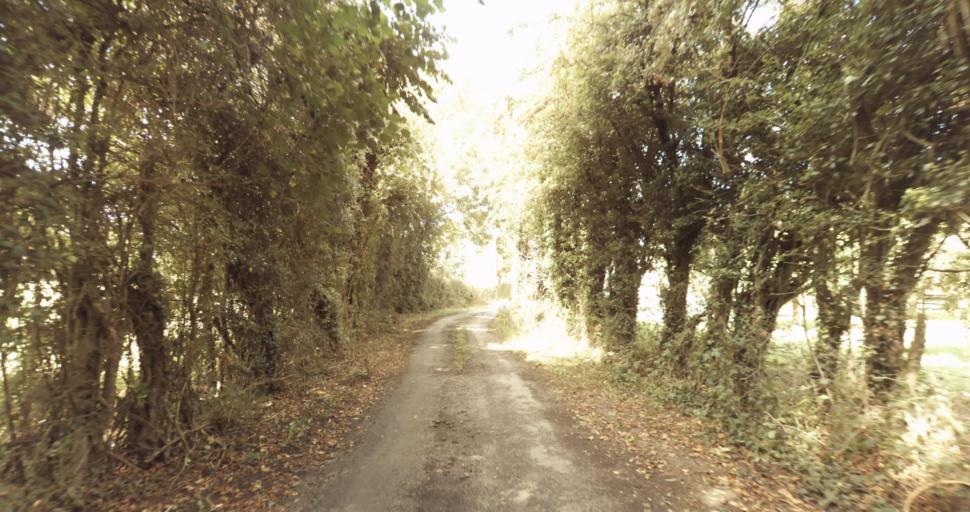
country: FR
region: Lower Normandy
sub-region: Departement de l'Orne
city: Gace
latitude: 48.8943
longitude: 0.3507
